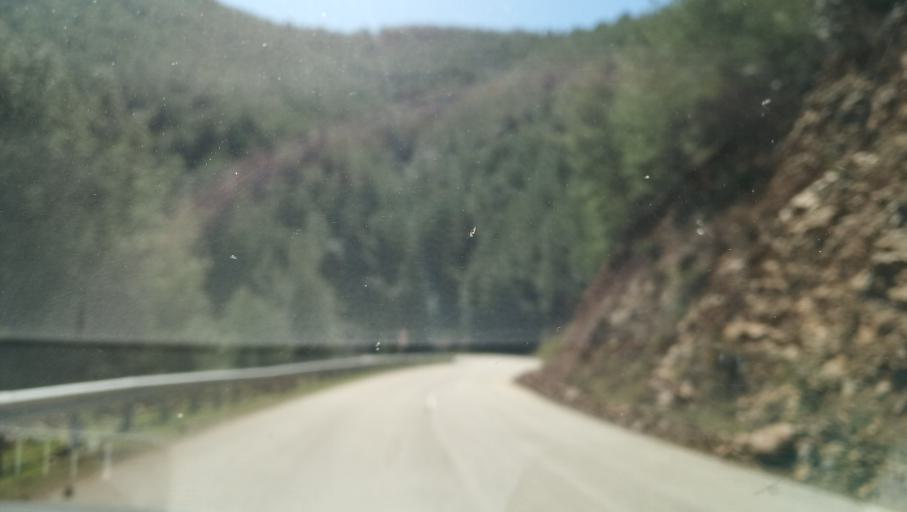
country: CY
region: Lefkosia
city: Lefka
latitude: 35.0685
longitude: 32.7542
